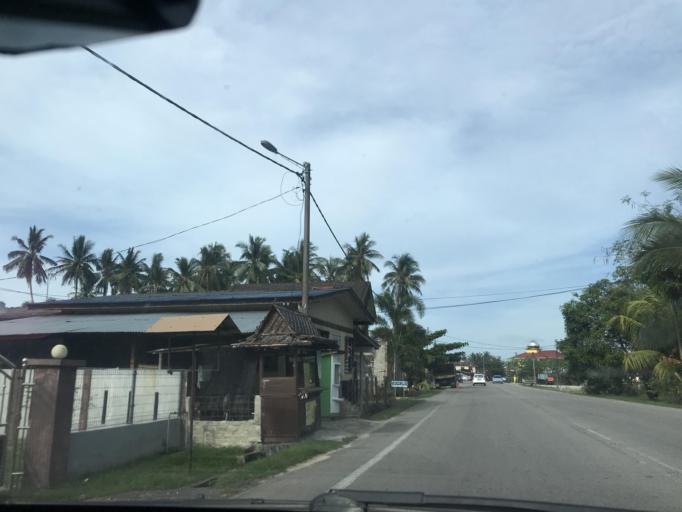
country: MY
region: Kelantan
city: Kota Bharu
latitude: 6.1379
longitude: 102.2105
